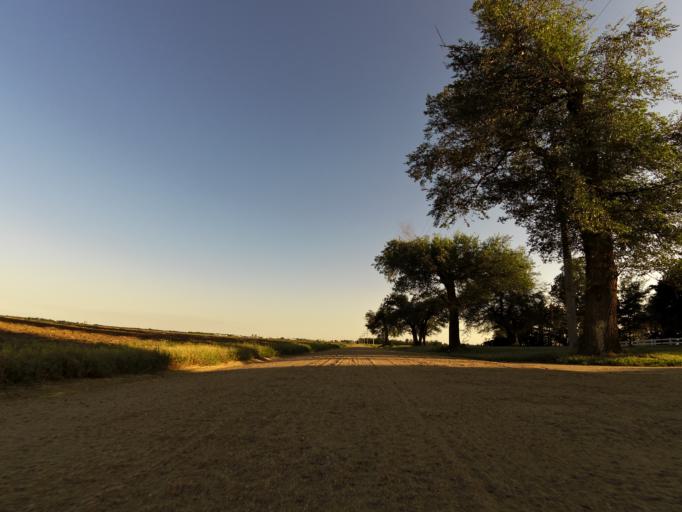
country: US
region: Kansas
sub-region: Reno County
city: South Hutchinson
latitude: 38.0132
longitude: -98.0320
